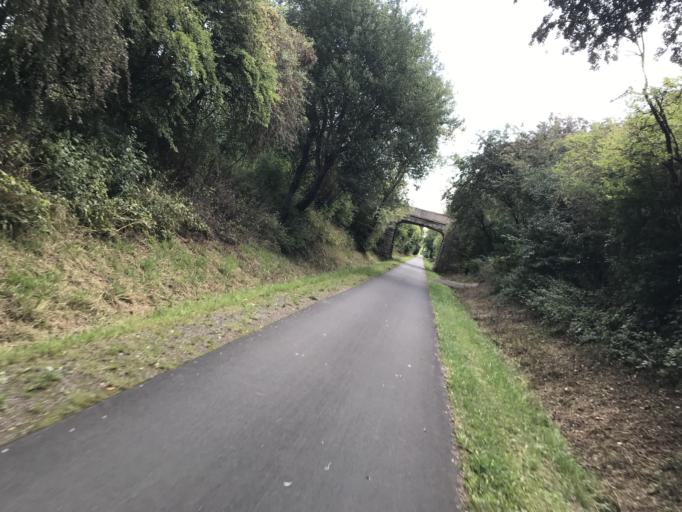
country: DE
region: Hesse
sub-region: Regierungsbezirk Kassel
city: Sachsenhausen
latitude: 51.2485
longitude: 9.0066
